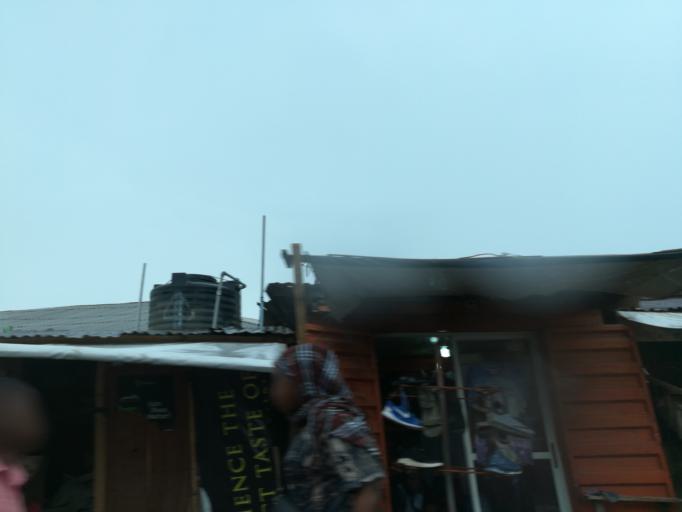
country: NG
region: Lagos
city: Oshodi
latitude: 6.5590
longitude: 3.3457
